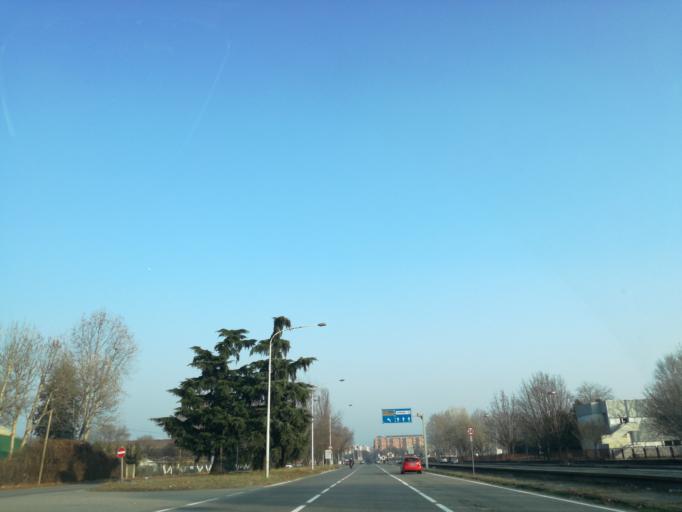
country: IT
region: Piedmont
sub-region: Provincia di Torino
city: Gerbido
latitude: 45.0512
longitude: 7.6117
